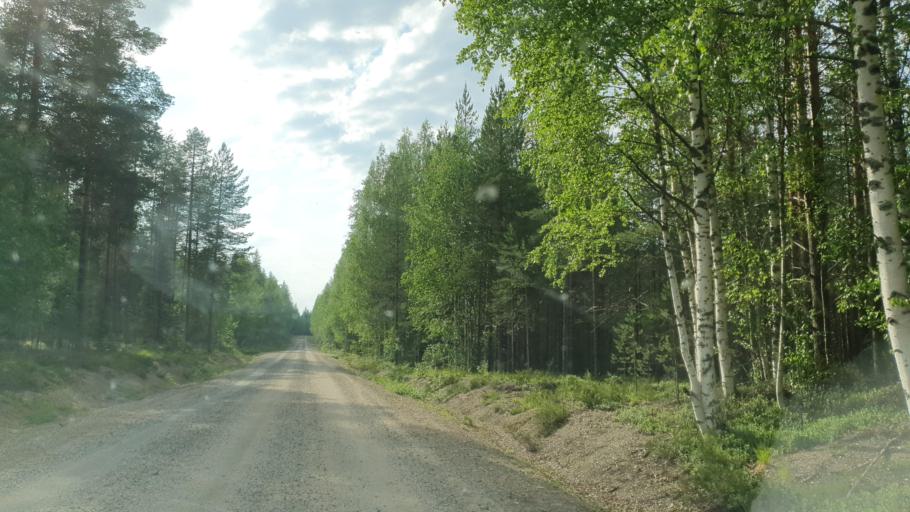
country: FI
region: Kainuu
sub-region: Kehys-Kainuu
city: Kuhmo
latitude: 64.0598
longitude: 29.7699
